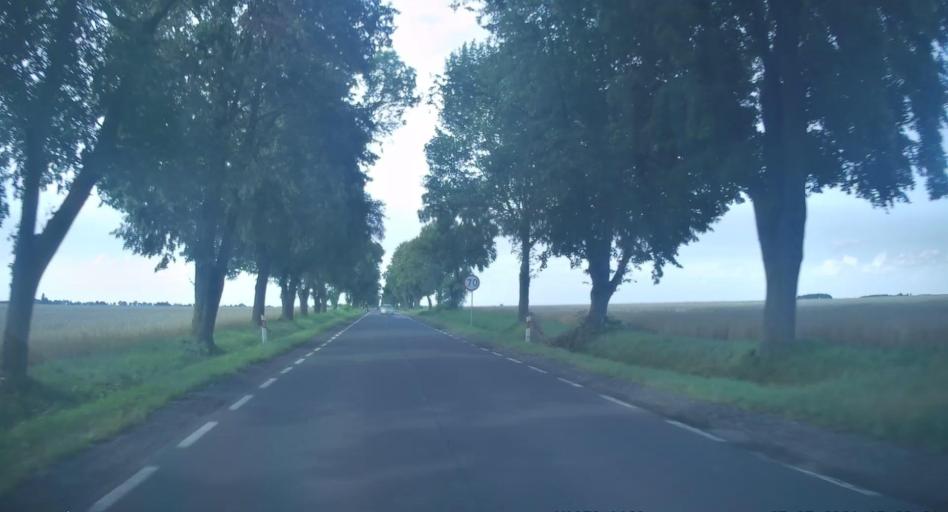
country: PL
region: Lodz Voivodeship
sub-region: Powiat tomaszowski
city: Rzeczyca
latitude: 51.6147
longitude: 20.2932
